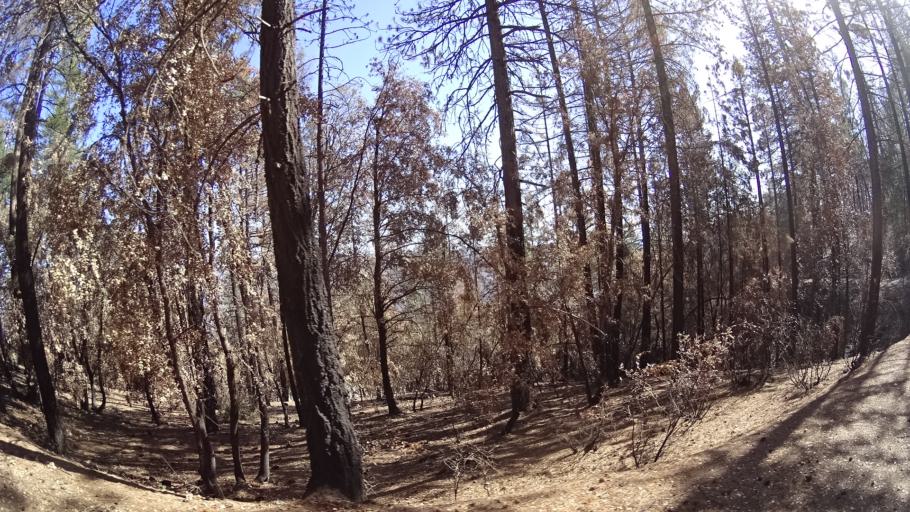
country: US
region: California
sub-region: Tehama County
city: Rancho Tehama Reserve
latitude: 39.6779
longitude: -122.7063
